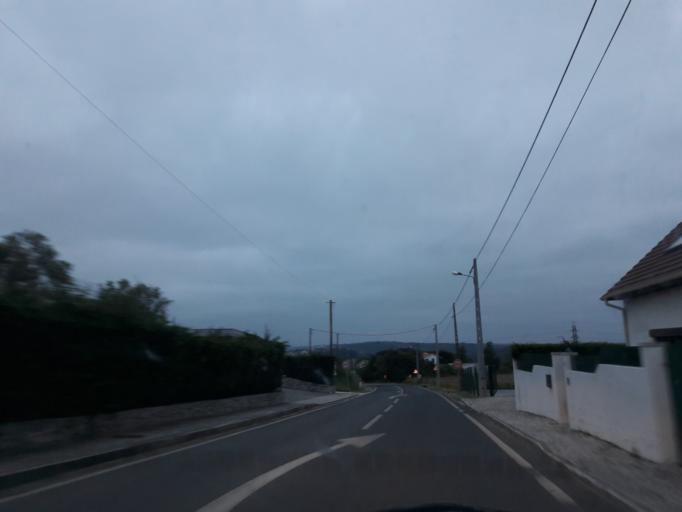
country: PT
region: Leiria
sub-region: Obidos
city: Obidos
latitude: 39.3729
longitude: -9.1320
